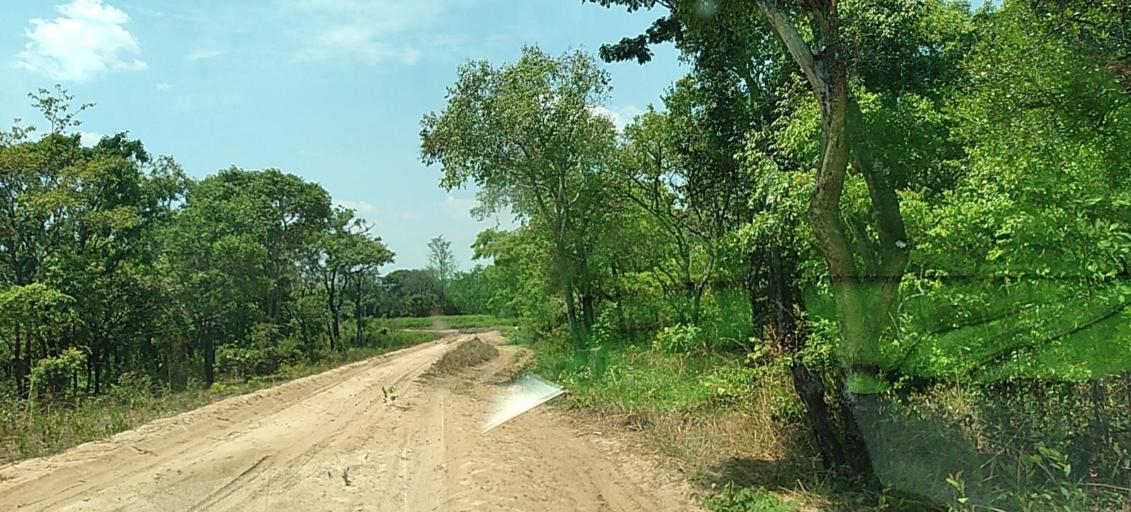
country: CD
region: Katanga
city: Kolwezi
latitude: -11.3141
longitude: 25.2355
